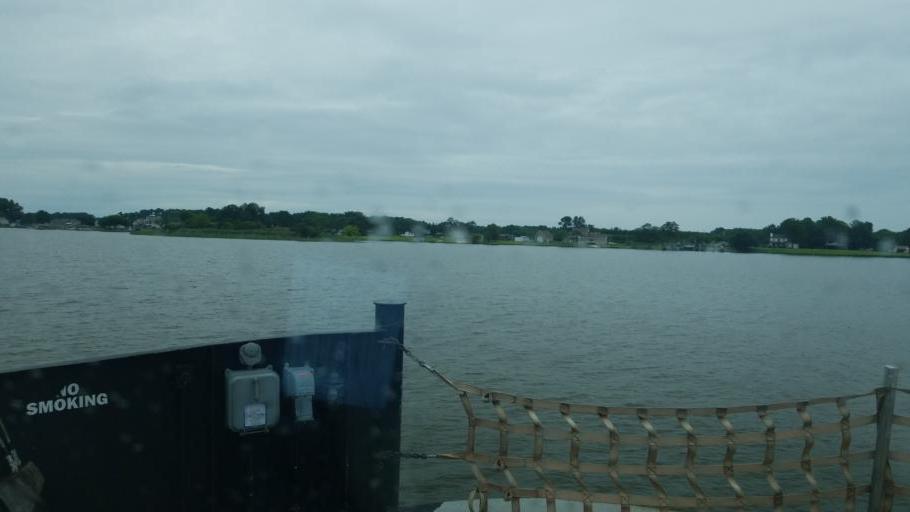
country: US
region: North Carolina
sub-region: Currituck County
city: Currituck
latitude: 36.4811
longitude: -75.9306
